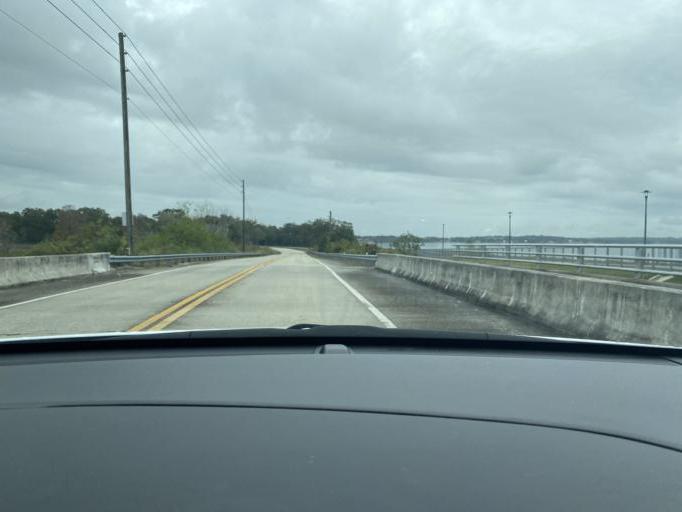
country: US
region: Florida
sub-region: Lake County
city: Clermont
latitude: 28.5656
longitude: -81.7771
